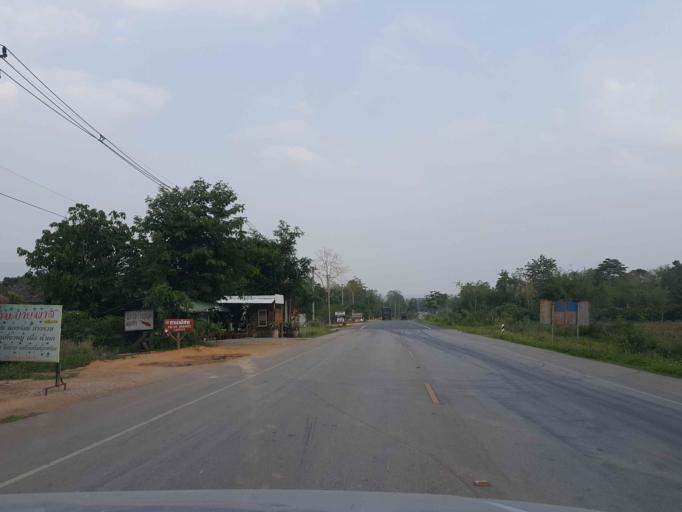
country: TH
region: Chiang Mai
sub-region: Amphoe Chiang Dao
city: Chiang Dao
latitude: 19.3741
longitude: 98.9469
